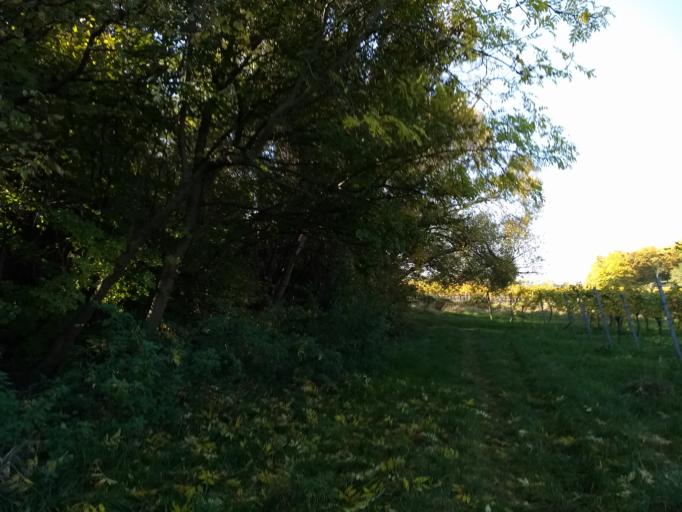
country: AT
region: Lower Austria
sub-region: Politischer Bezirk Modling
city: Perchtoldsdorf
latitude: 48.1049
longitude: 16.2551
